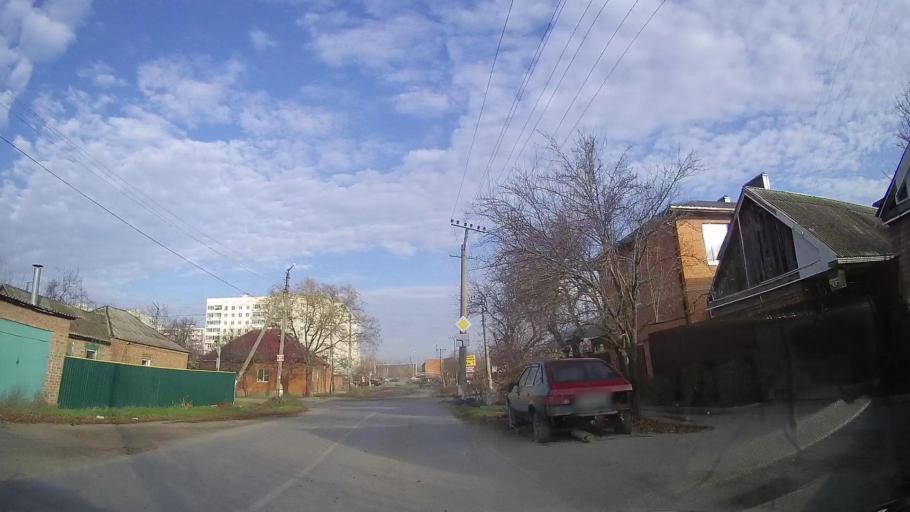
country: RU
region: Rostov
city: Bataysk
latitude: 47.1333
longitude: 39.7737
